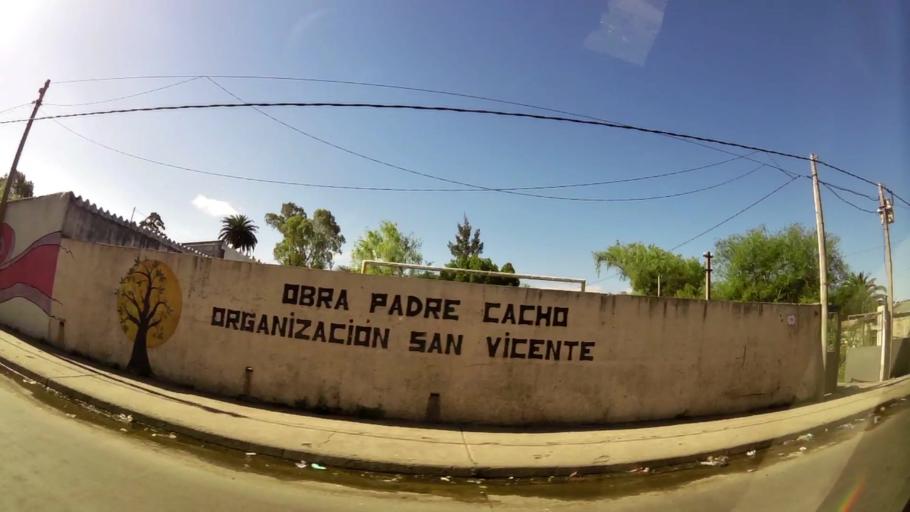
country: UY
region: Montevideo
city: Montevideo
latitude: -34.8347
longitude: -56.1599
